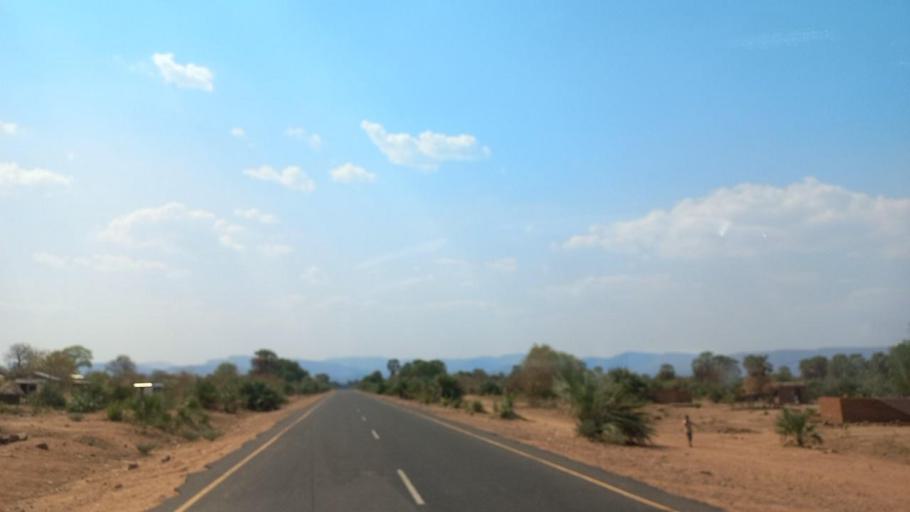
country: ZM
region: Lusaka
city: Luangwa
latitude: -15.1124
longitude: 30.2037
